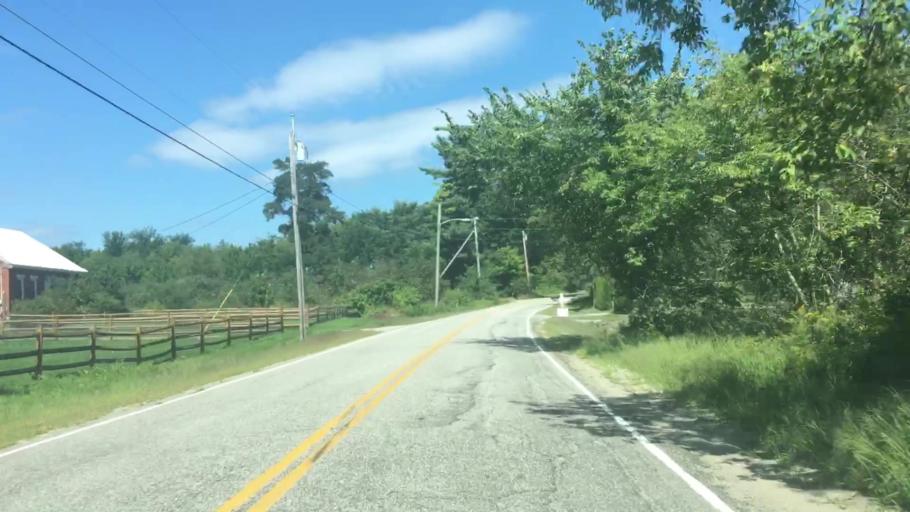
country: US
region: Maine
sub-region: Kennebec County
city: Monmouth
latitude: 44.1352
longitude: -69.9645
